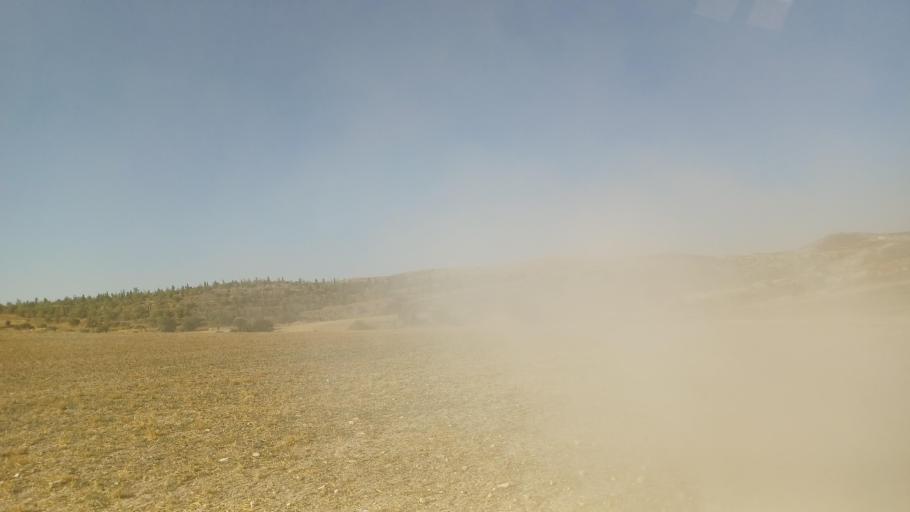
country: CY
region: Larnaka
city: Athienou
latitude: 35.0287
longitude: 33.5449
